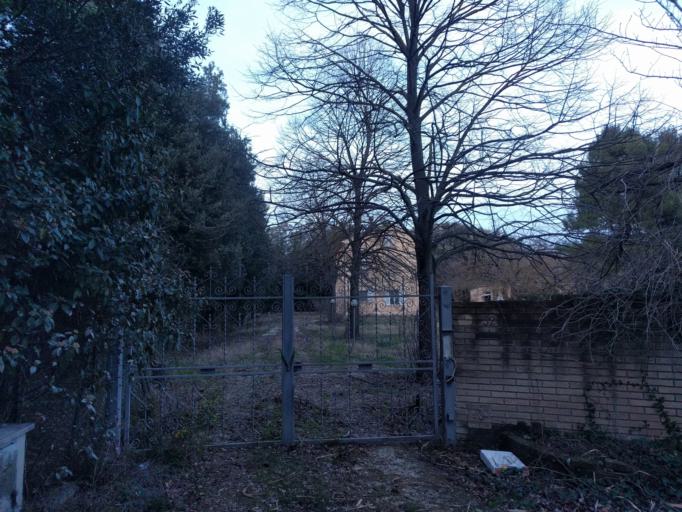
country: IT
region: The Marches
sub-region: Provincia di Pesaro e Urbino
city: Fano
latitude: 43.8133
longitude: 13.0370
